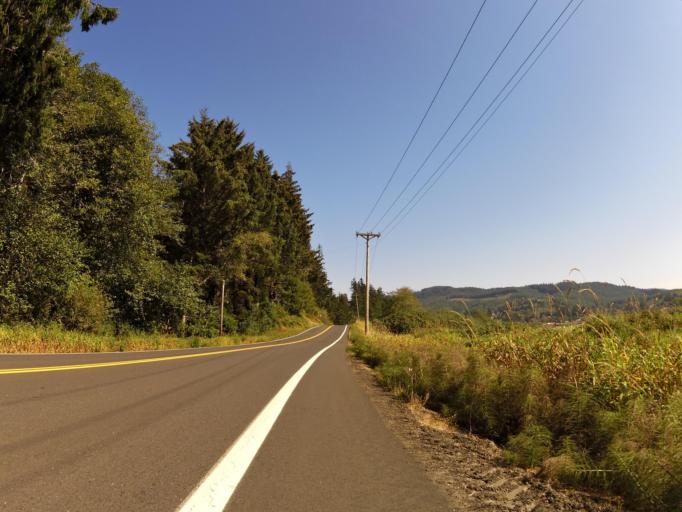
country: US
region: Oregon
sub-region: Tillamook County
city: Pacific City
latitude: 45.1807
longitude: -123.9407
